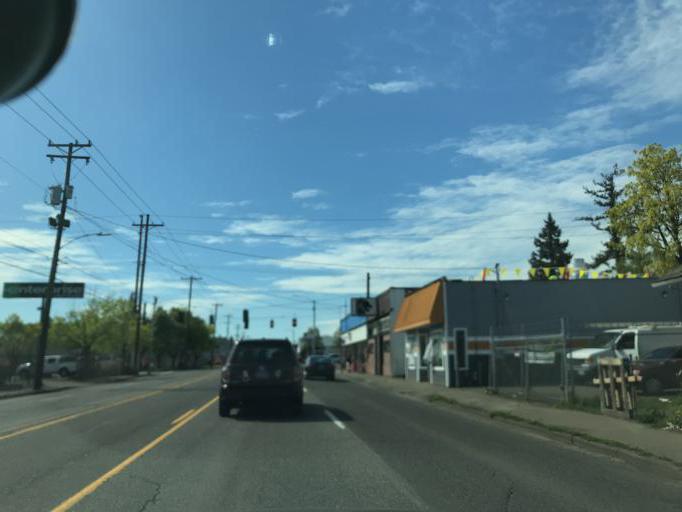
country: US
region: Oregon
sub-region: Multnomah County
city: Lents
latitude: 45.4802
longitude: -122.5791
